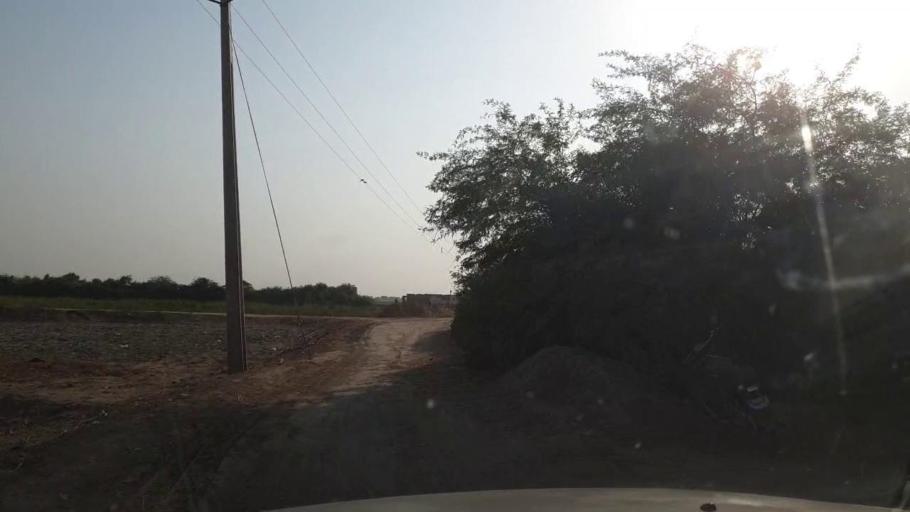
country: PK
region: Sindh
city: Bulri
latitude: 24.9522
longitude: 68.3423
